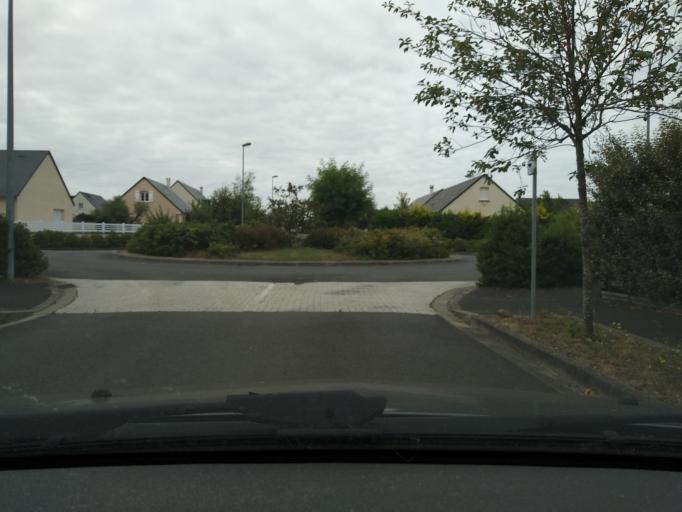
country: FR
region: Centre
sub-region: Departement d'Indre-et-Loire
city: Chanceaux-sur-Choisille
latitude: 47.4539
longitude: 0.7018
